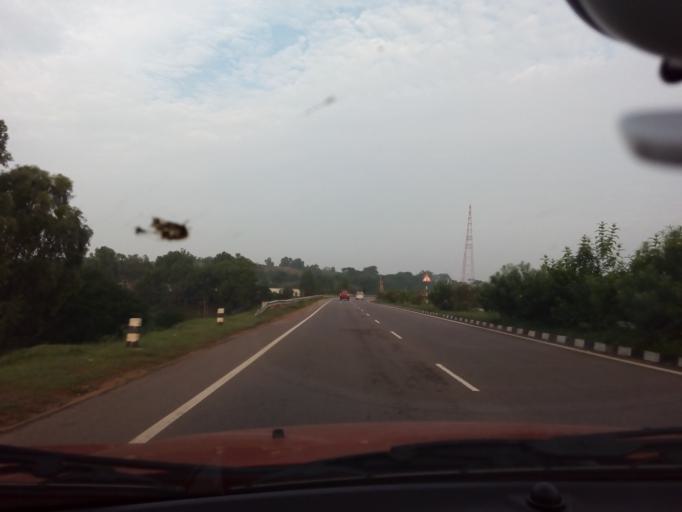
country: IN
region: Karnataka
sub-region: Ramanagara
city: Magadi
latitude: 13.0733
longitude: 77.2226
